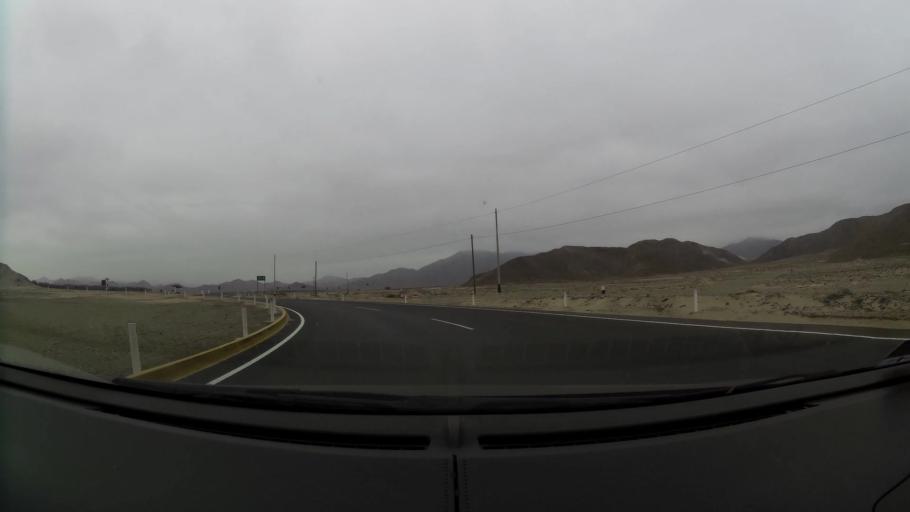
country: PE
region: La Libertad
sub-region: Viru
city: Chao
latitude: -8.6484
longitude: -78.6212
